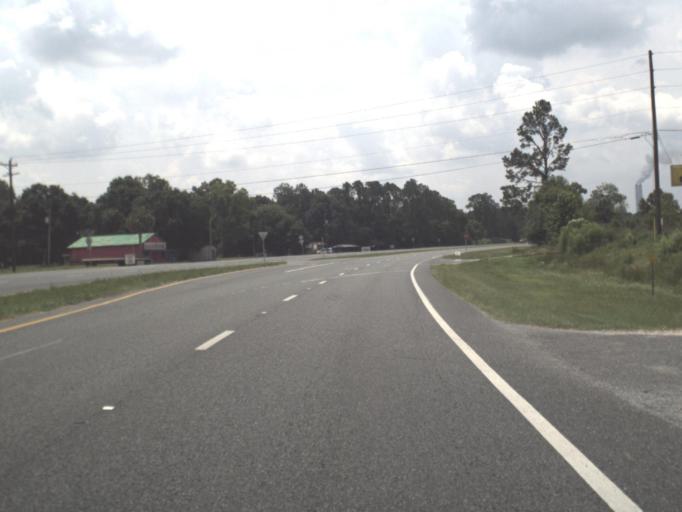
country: US
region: Florida
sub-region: Putnam County
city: East Palatka
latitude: 29.7740
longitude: -81.6396
